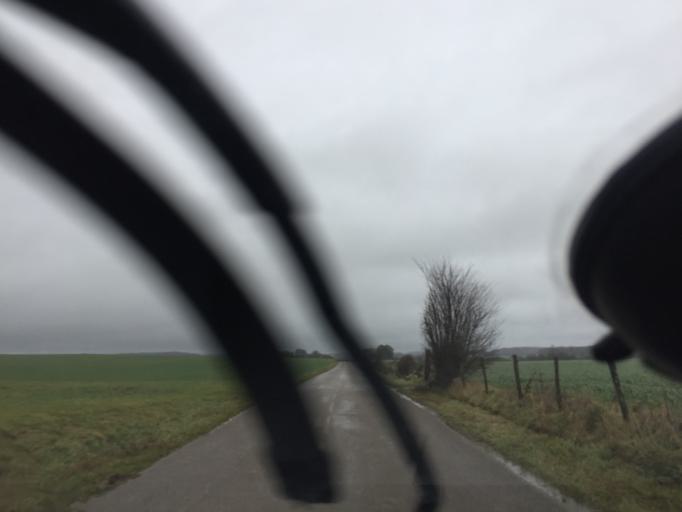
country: FR
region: Franche-Comte
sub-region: Departement du Jura
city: Orchamps
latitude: 47.1536
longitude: 5.6151
